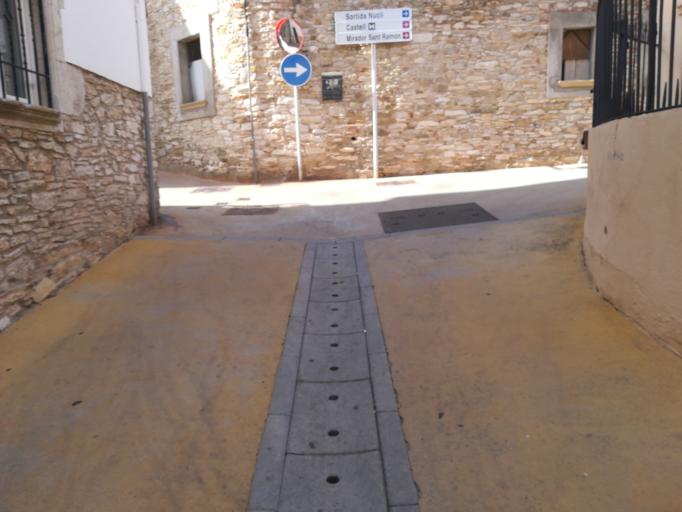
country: ES
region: Catalonia
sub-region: Provincia de Girona
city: Begur
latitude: 41.9551
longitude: 3.2092
